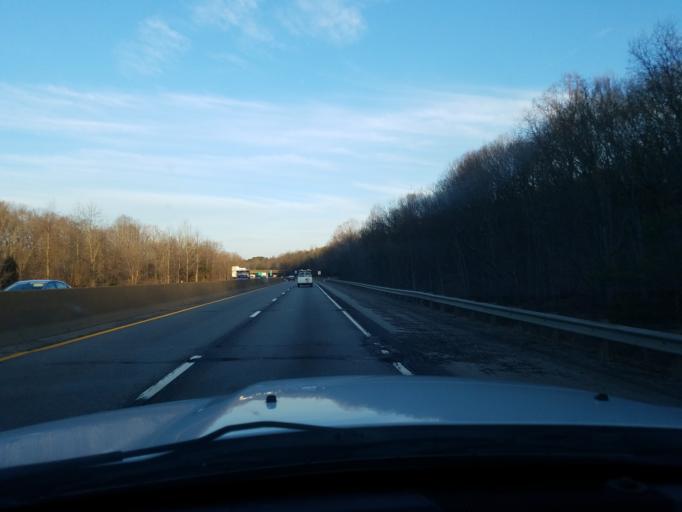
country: US
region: West Virginia
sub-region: Kanawha County
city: Nitro
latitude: 38.4514
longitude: -81.8563
